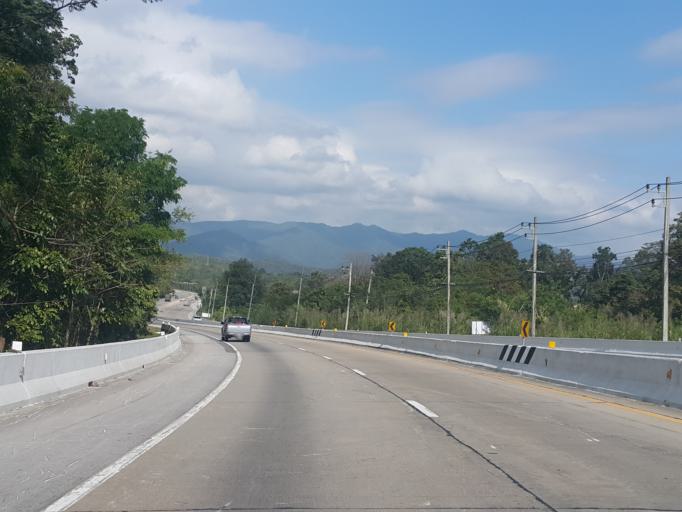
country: TH
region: Lamphun
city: Mae Tha
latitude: 18.4446
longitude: 99.2049
